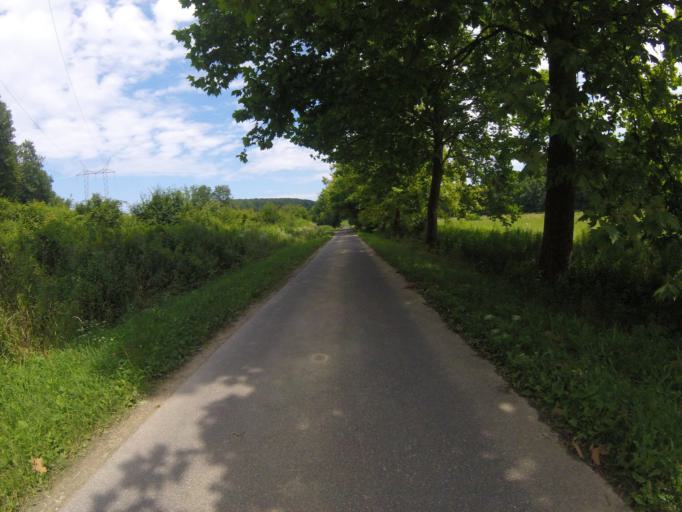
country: HU
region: Zala
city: Lenti
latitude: 46.5642
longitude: 16.6299
